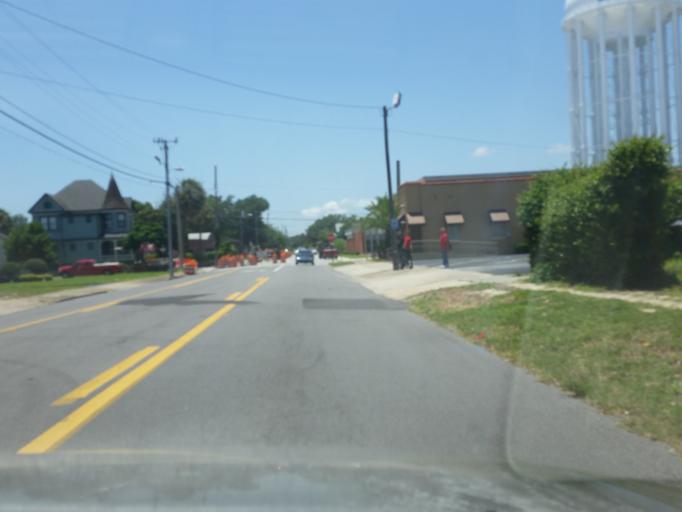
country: US
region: Florida
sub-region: Escambia County
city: Pensacola
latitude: 30.4151
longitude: -87.2180
